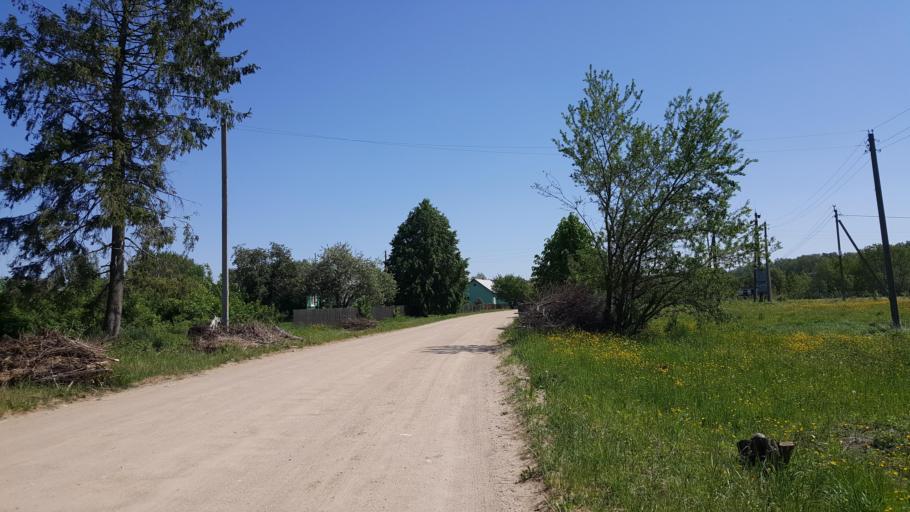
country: BY
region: Brest
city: Charnawchytsy
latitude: 52.2738
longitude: 23.7718
